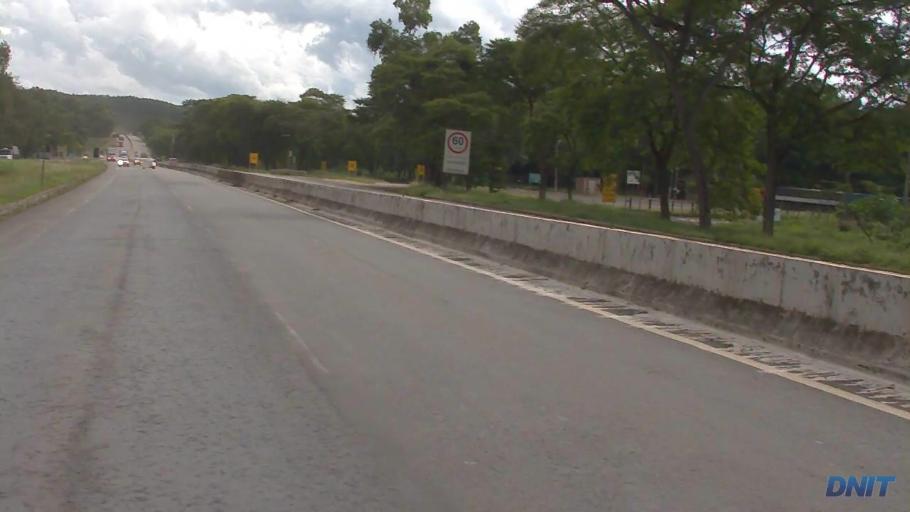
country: BR
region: Minas Gerais
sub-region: Ipaba
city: Ipaba
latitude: -19.3141
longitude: -42.3977
